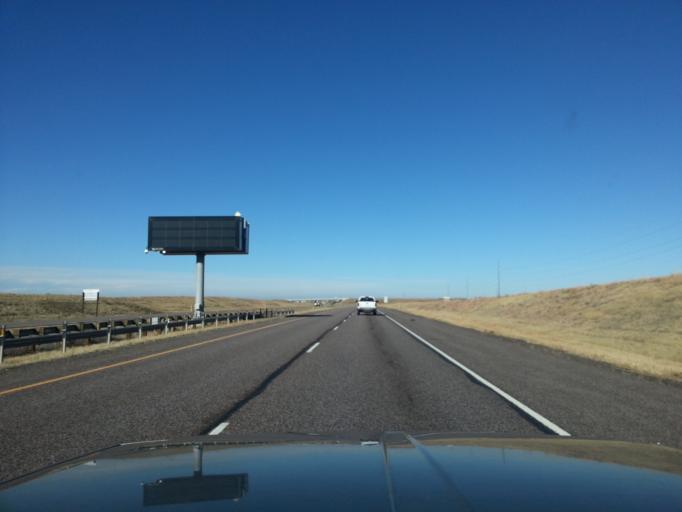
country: US
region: Colorado
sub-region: Adams County
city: Brighton
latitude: 39.8924
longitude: -104.7617
